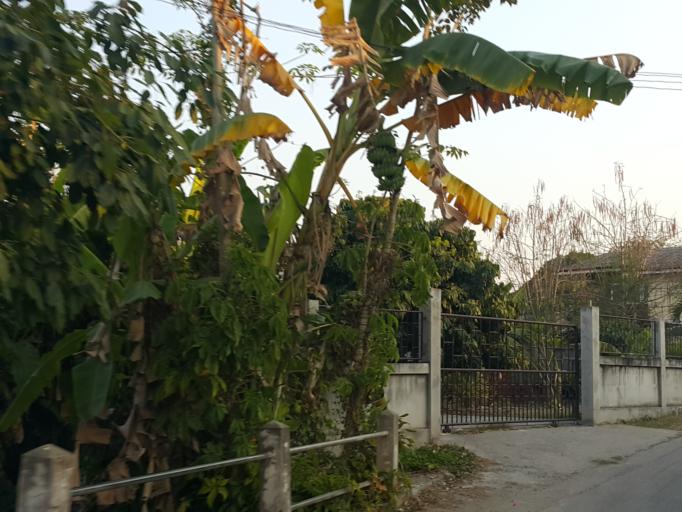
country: TH
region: Chiang Mai
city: San Sai
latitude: 18.8932
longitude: 98.9609
